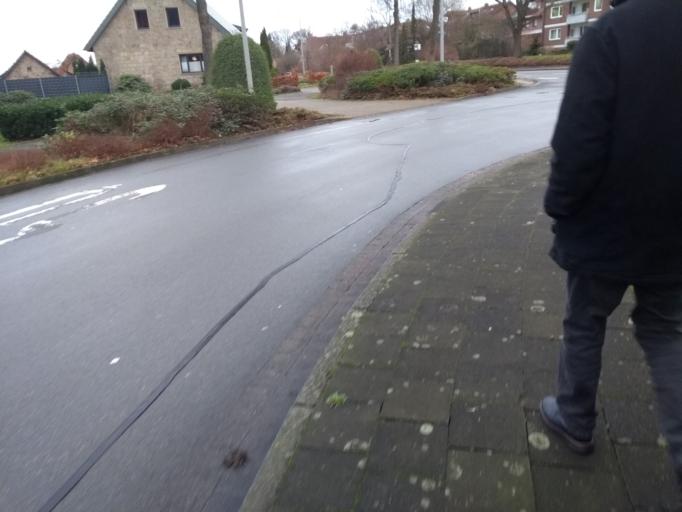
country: DE
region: North Rhine-Westphalia
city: Ibbenburen
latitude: 52.2828
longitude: 7.7018
